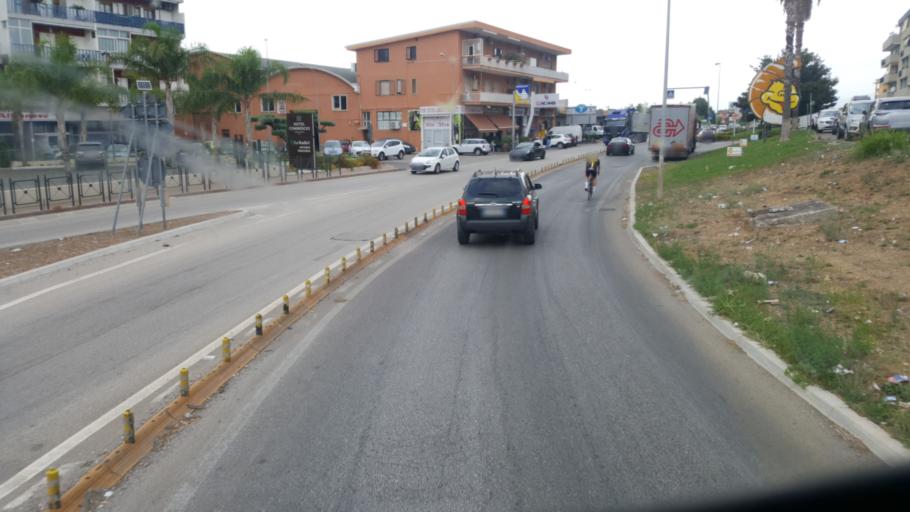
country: IT
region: Campania
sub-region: Provincia di Salerno
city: Battipaglia
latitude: 40.6014
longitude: 14.9760
